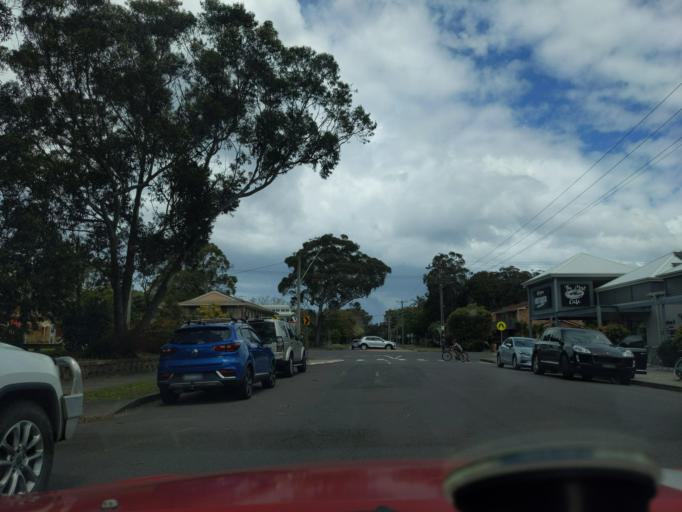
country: AU
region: New South Wales
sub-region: Great Lakes
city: Hawks Nest
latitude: -32.6722
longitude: 152.1774
